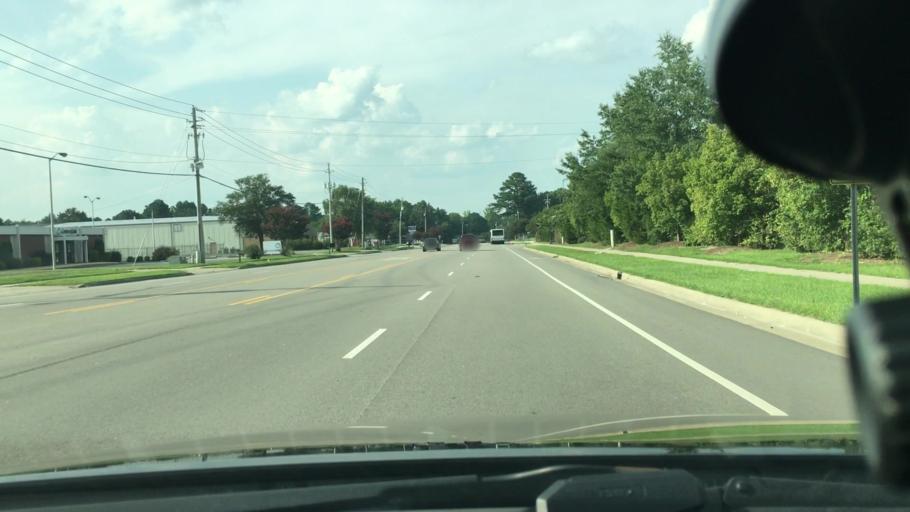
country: US
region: North Carolina
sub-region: Pitt County
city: Summerfield
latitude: 35.5756
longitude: -77.3902
